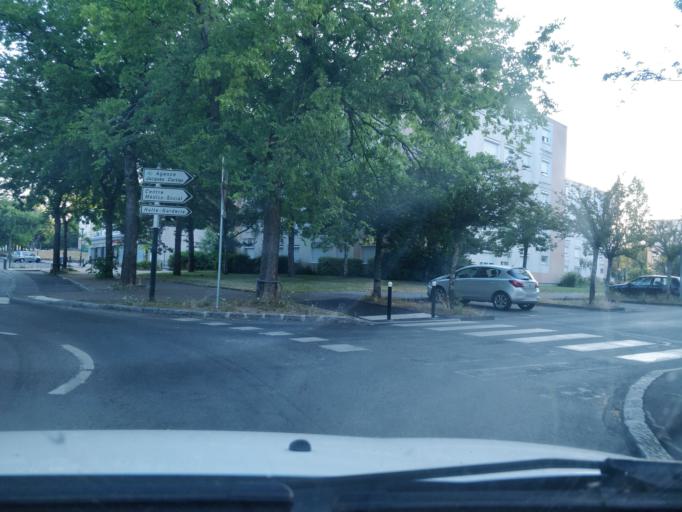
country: FR
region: Pays de la Loire
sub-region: Departement de la Loire-Atlantique
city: La Chapelle-sur-Erdre
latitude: 47.2587
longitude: -1.5751
